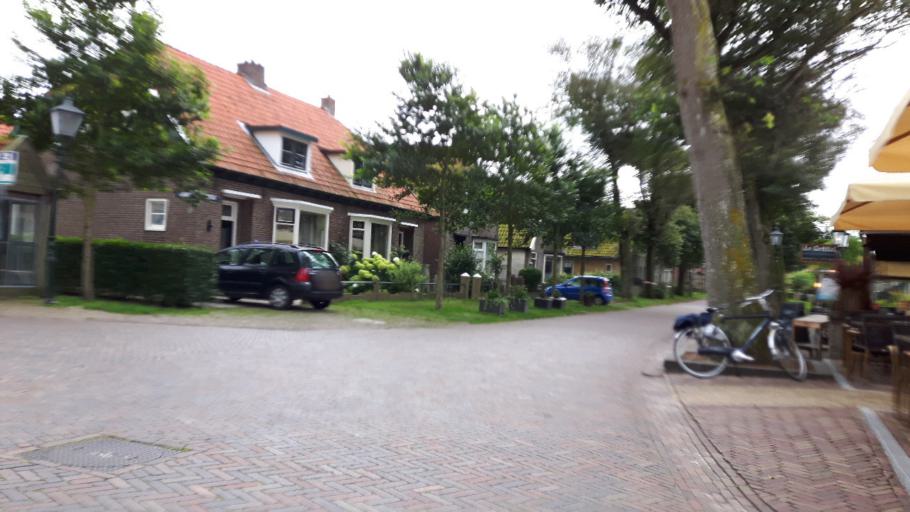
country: NL
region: Friesland
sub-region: Gemeente Ameland
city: Hollum
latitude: 53.4384
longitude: 5.6397
